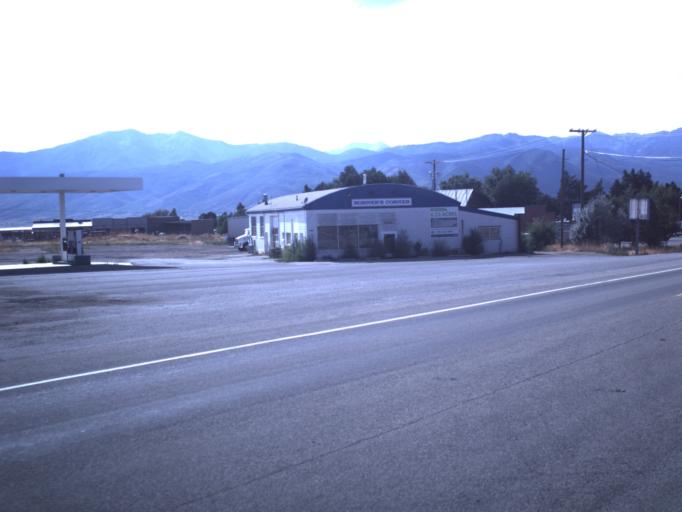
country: US
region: Utah
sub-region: Wasatch County
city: Heber
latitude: 40.4887
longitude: -111.4089
